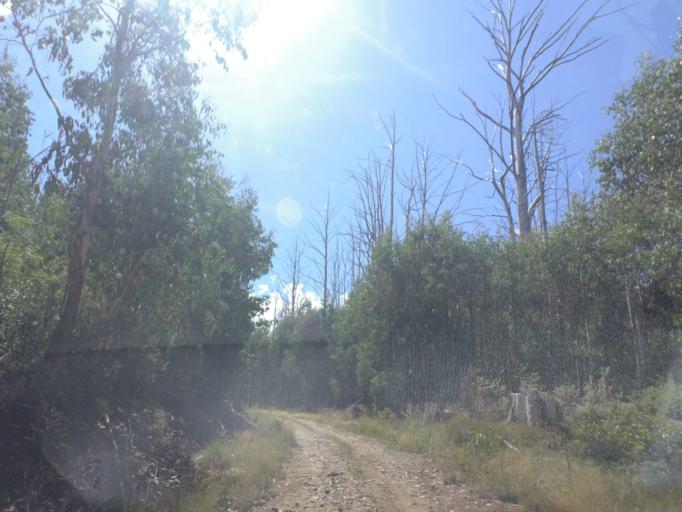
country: AU
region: Victoria
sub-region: Murrindindi
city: Alexandra
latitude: -37.4655
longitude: 145.8349
